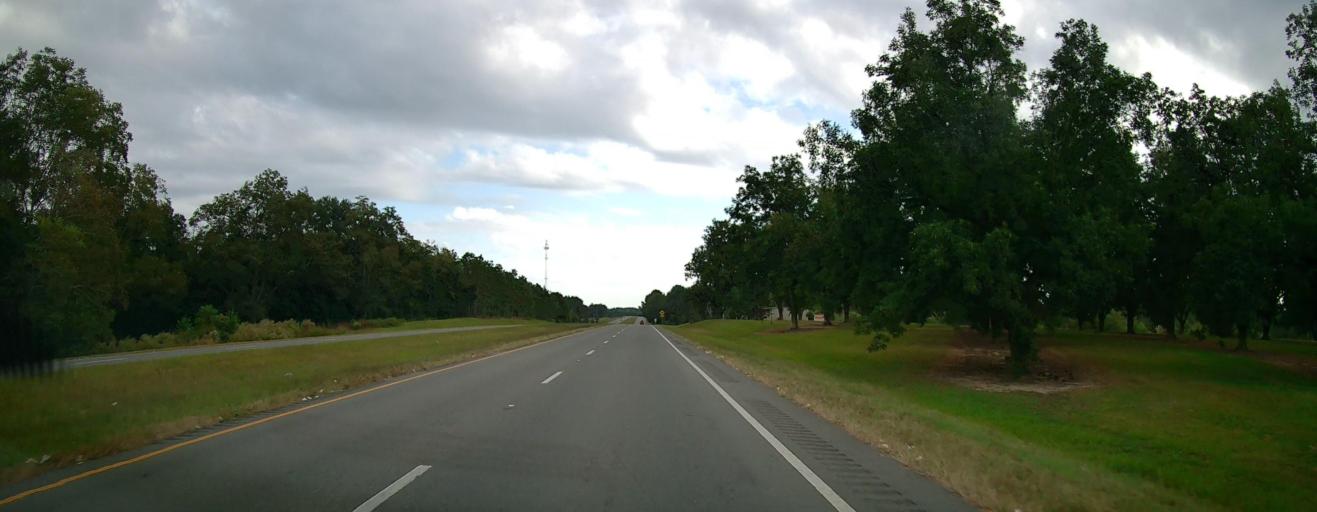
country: US
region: Georgia
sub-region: Thomas County
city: Meigs
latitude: 31.0718
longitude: -84.0778
